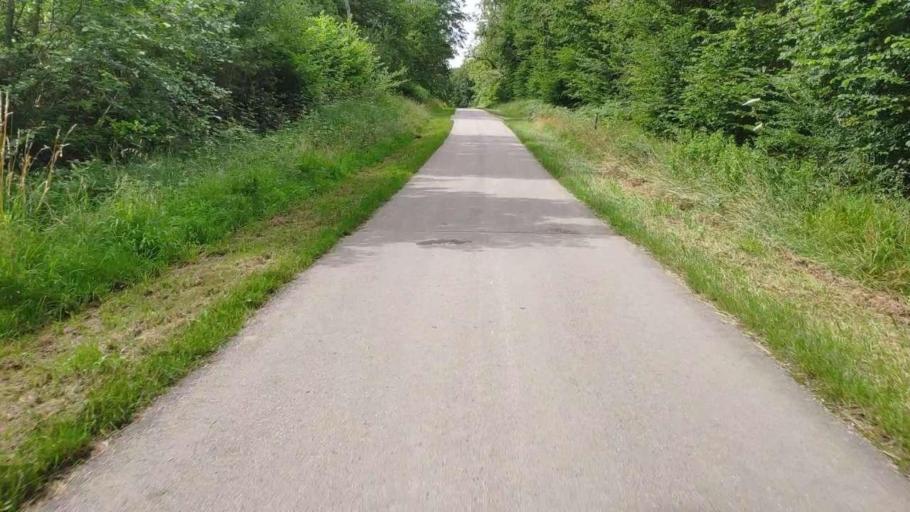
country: FR
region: Franche-Comte
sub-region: Departement du Jura
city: Bletterans
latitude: 46.8094
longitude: 5.4403
